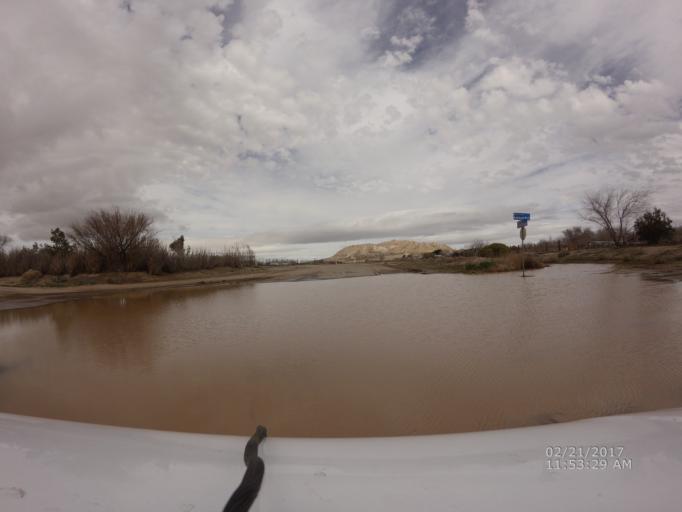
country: US
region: California
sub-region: Los Angeles County
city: Lake Los Angeles
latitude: 34.6347
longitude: -117.8541
